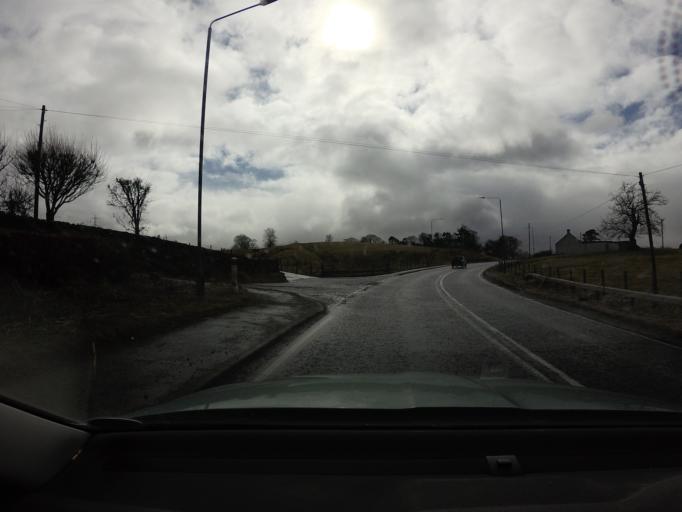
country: GB
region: Scotland
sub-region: South Lanarkshire
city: Douglas
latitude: 55.5808
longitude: -3.8058
